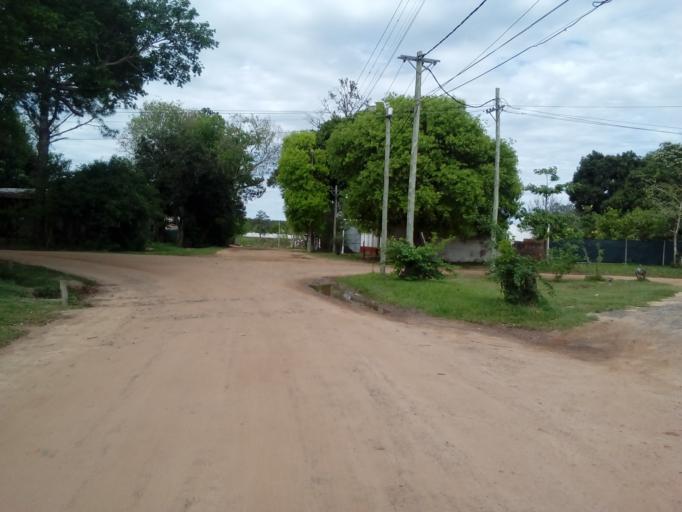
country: AR
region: Corrientes
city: San Luis del Palmar
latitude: -27.4585
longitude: -58.6526
